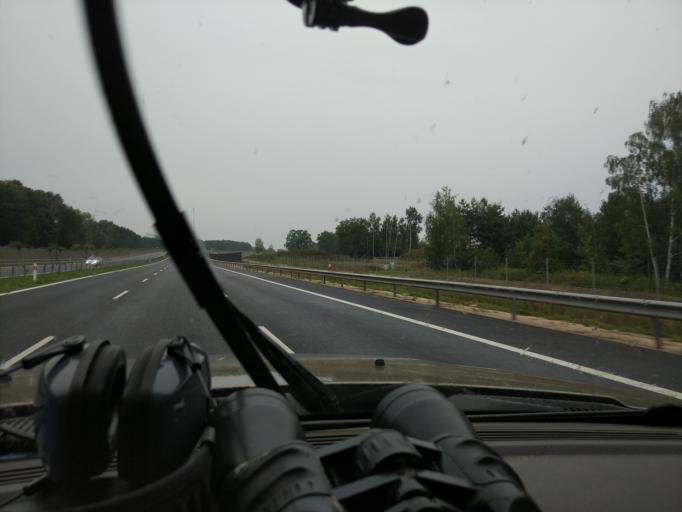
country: PL
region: Masovian Voivodeship
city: Zielonka
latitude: 52.3397
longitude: 21.1566
